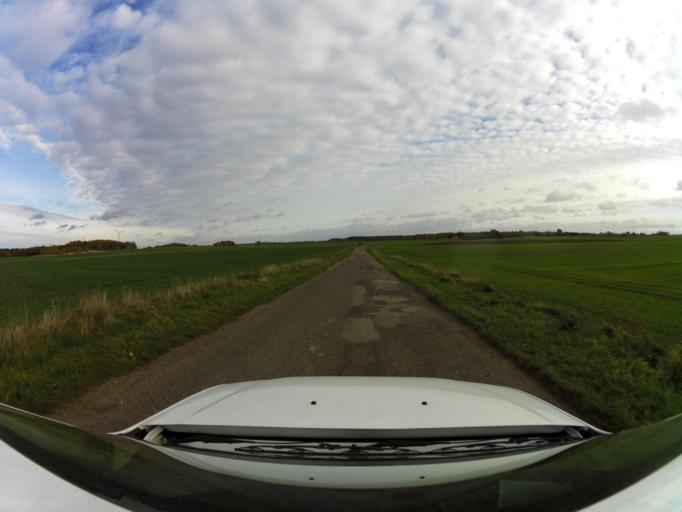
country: PL
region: West Pomeranian Voivodeship
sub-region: Powiat gryficki
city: Gryfice
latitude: 54.0009
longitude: 15.2027
